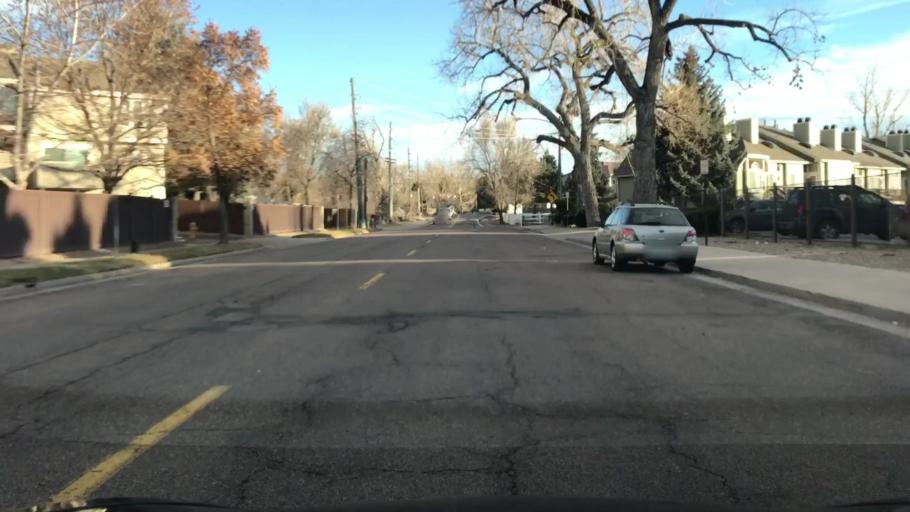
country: US
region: Colorado
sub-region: Arapahoe County
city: Glendale
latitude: 39.6832
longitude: -104.8901
